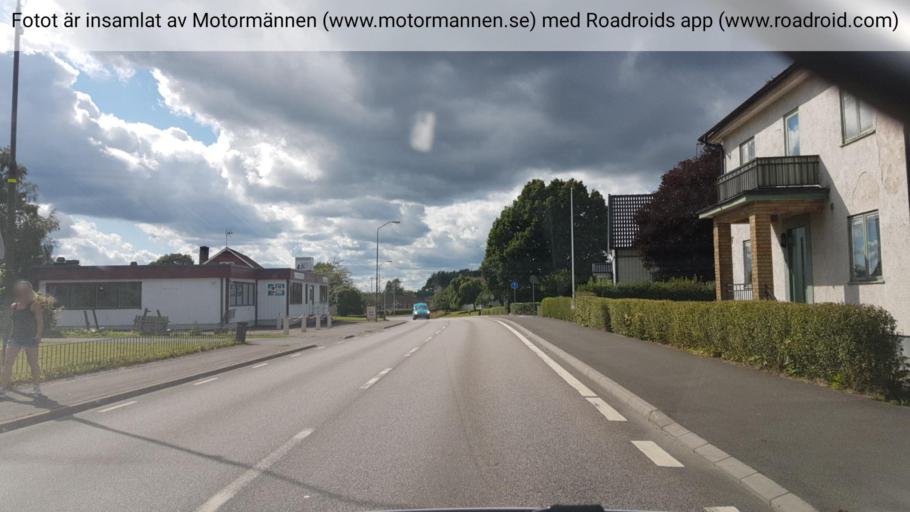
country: SE
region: Vaestra Goetaland
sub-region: Falkopings Kommun
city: Falkoeping
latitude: 58.0244
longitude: 13.5649
